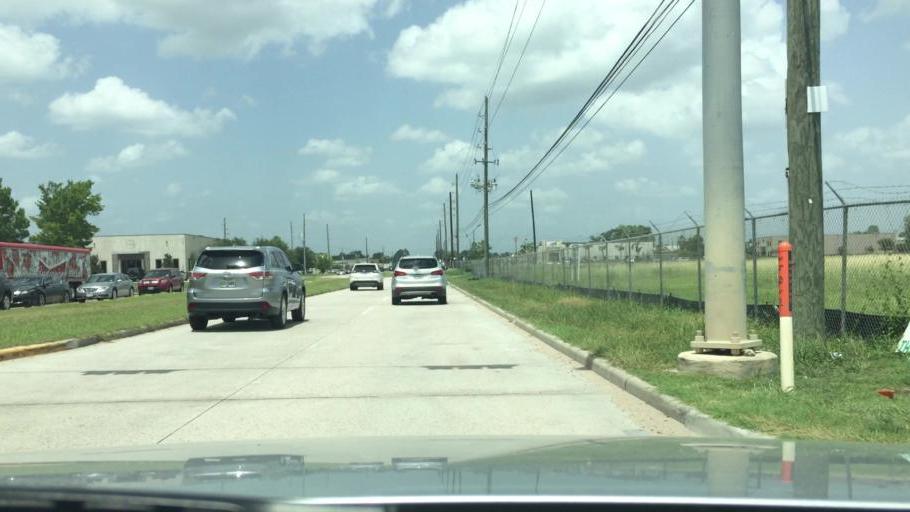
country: US
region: Texas
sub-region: Harris County
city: Hudson
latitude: 29.9564
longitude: -95.5249
